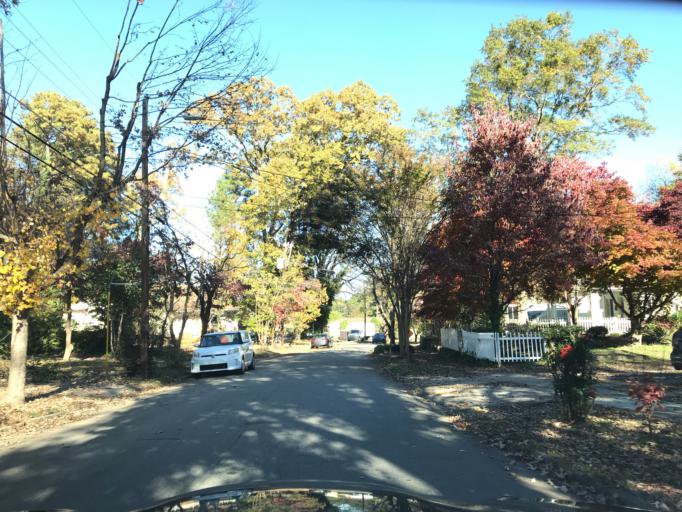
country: US
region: North Carolina
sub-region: Wake County
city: Raleigh
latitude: 35.7984
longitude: -78.6315
